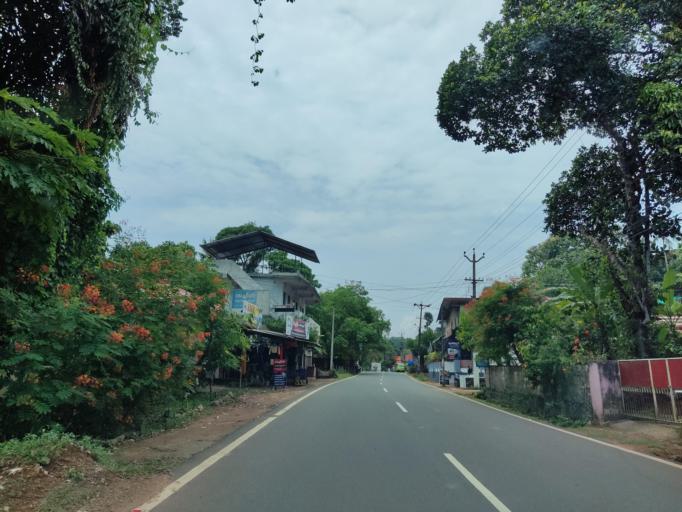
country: IN
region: Kerala
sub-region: Alappuzha
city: Chengannur
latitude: 9.2867
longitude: 76.6153
